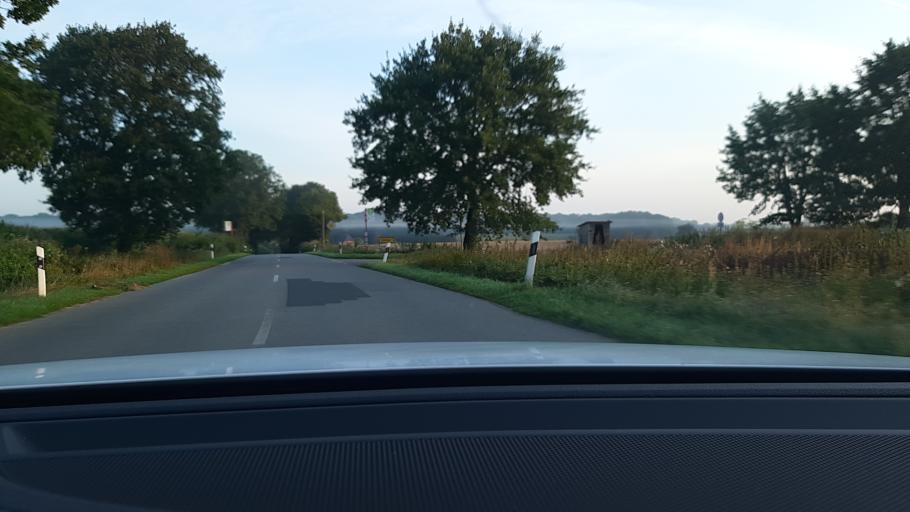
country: DE
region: Schleswig-Holstein
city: Wesenberg
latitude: 53.8263
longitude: 10.5382
